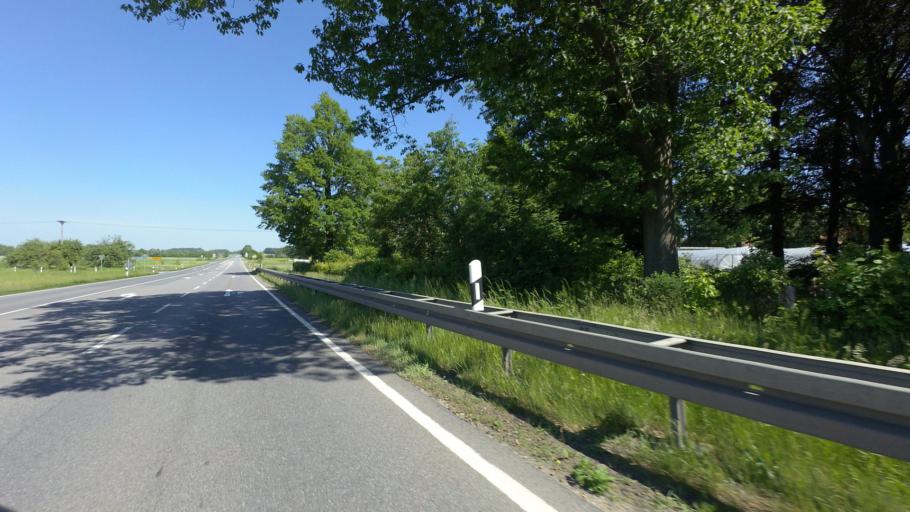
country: DE
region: Brandenburg
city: Spremberg
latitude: 51.6583
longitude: 14.3601
